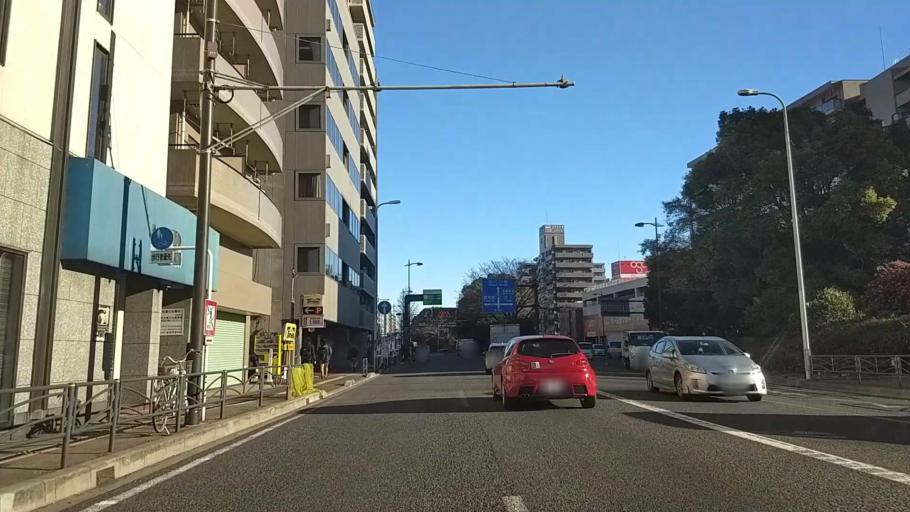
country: JP
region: Kanagawa
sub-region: Kawasaki-shi
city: Kawasaki
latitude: 35.5048
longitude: 139.6785
